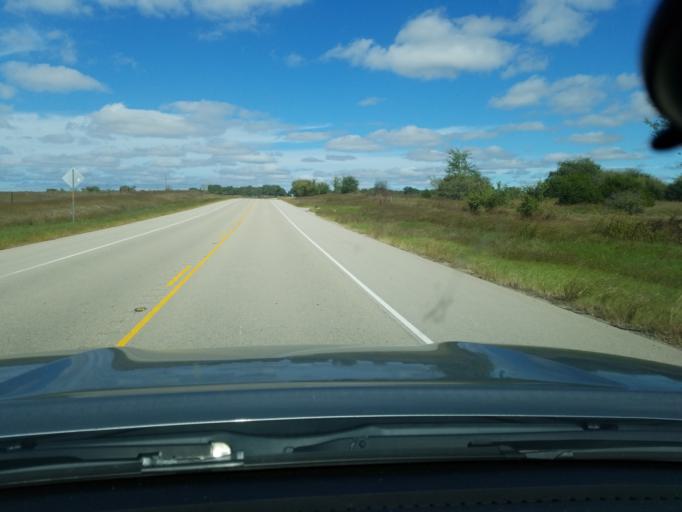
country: US
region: Texas
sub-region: Hamilton County
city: Hamilton
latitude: 31.6099
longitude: -98.1588
